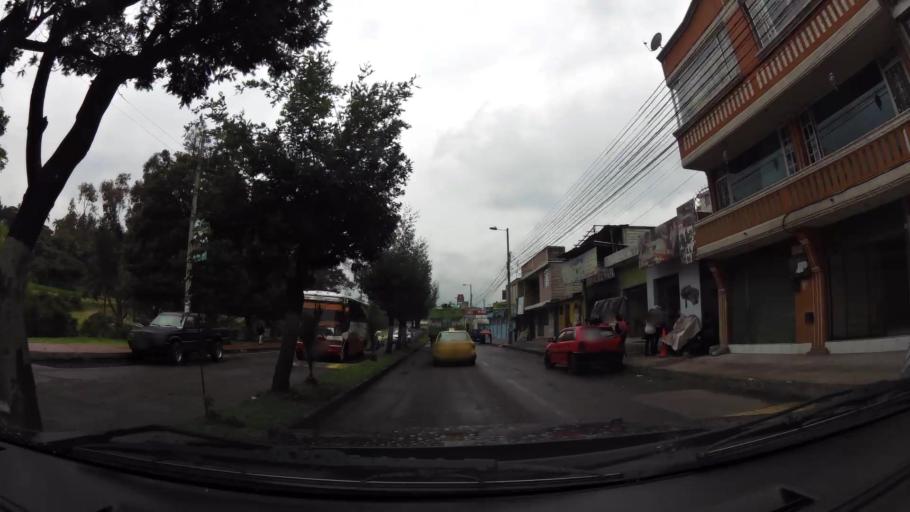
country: EC
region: Pichincha
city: Sangolqui
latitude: -0.3321
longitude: -78.4419
